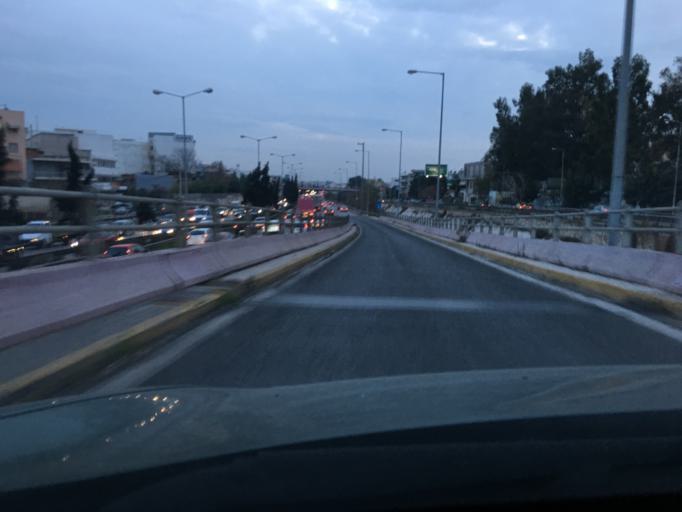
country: GR
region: Attica
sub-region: Nomarchia Athinas
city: Nea Chalkidona
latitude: 38.0303
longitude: 23.7282
